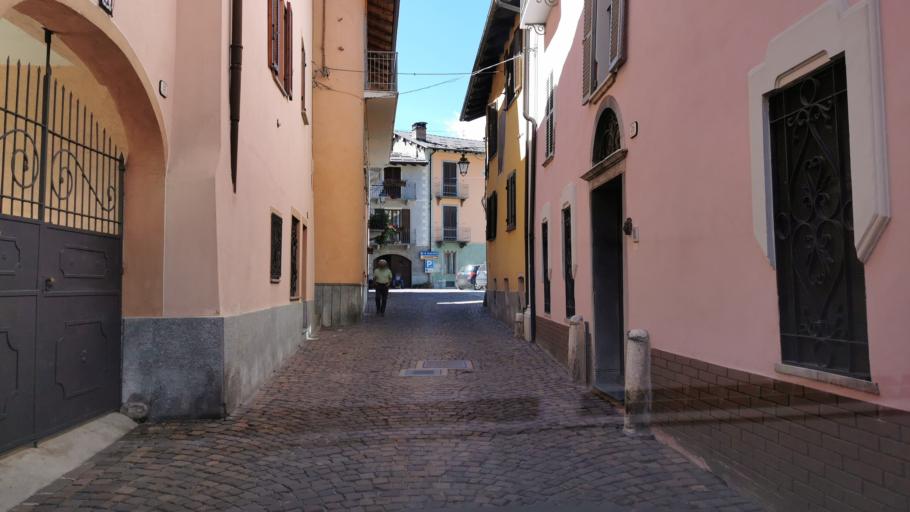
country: IT
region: Piedmont
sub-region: Provincia di Cuneo
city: Entracque
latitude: 44.2387
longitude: 7.3964
